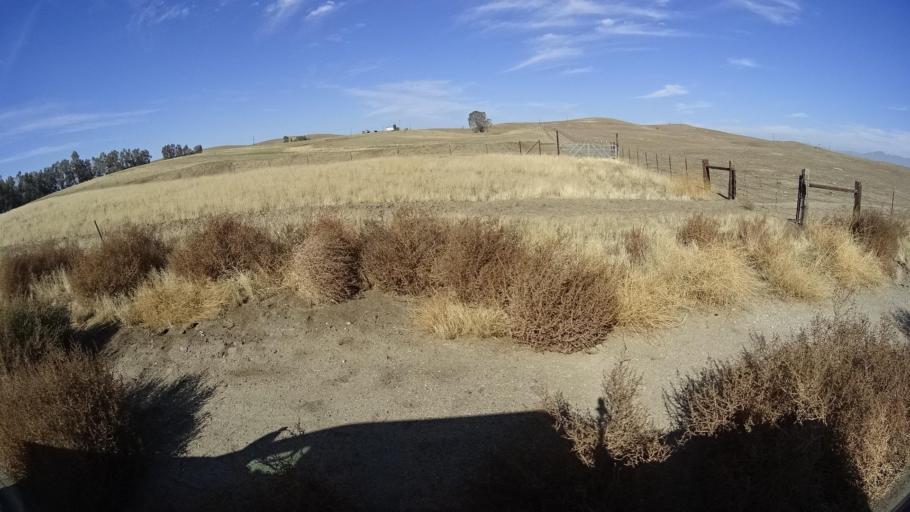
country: US
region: California
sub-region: Kern County
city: Oildale
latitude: 35.6308
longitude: -118.9668
